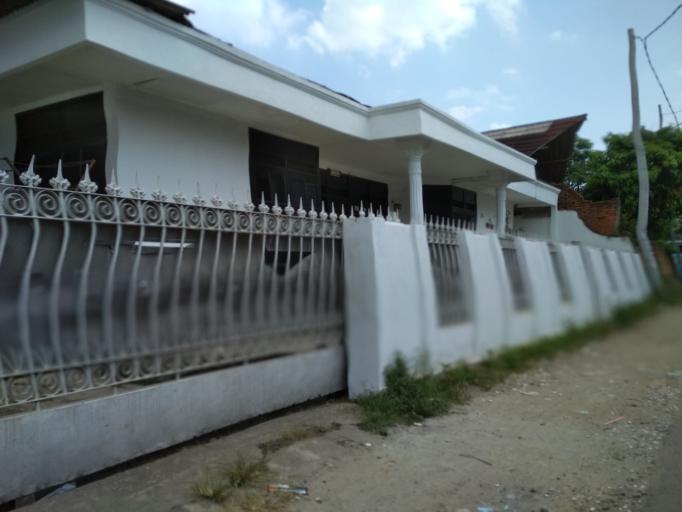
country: ID
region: West Java
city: Ciampea
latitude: -6.5587
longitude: 106.7358
